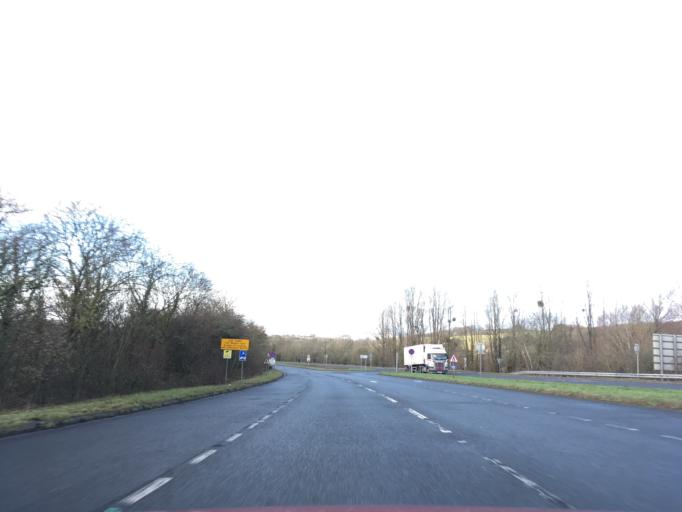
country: GB
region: Wales
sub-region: Monmouthshire
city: Usk
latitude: 51.7048
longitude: -2.8752
